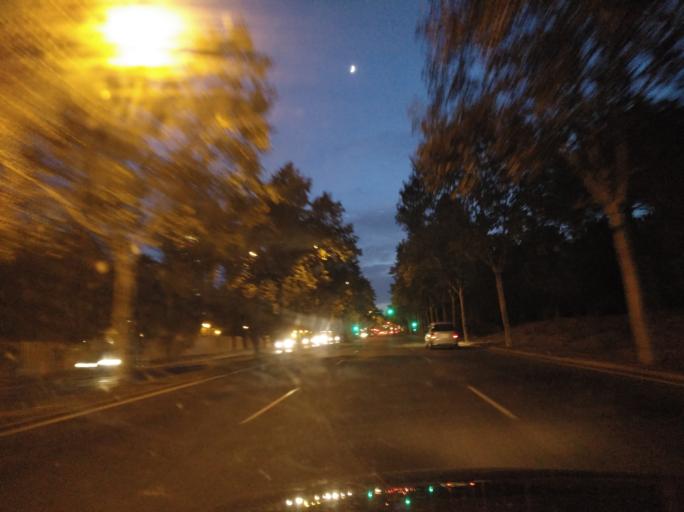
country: ES
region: Andalusia
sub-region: Provincia de Sevilla
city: Camas
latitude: 37.3989
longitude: -6.0117
